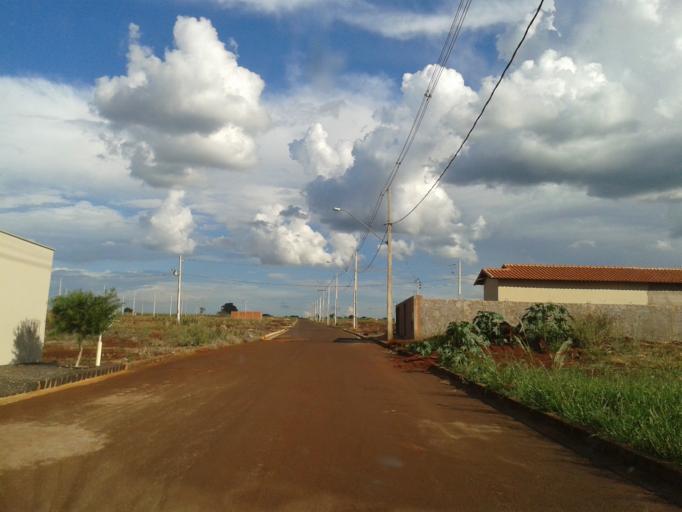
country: BR
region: Minas Gerais
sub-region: Capinopolis
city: Capinopolis
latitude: -18.6928
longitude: -49.5766
